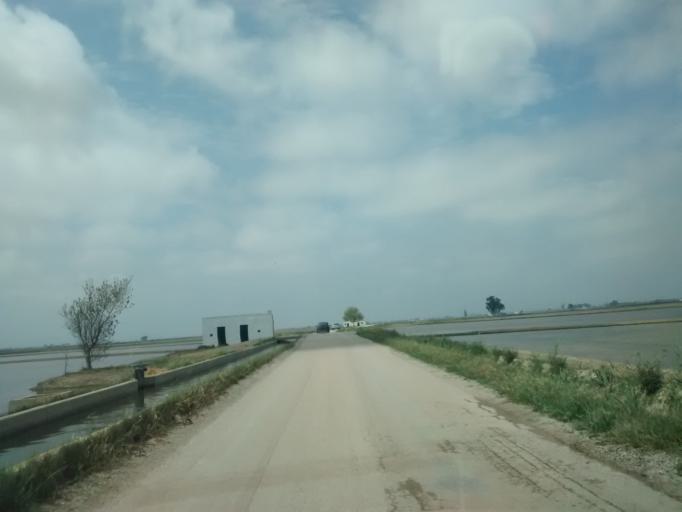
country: ES
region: Catalonia
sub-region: Provincia de Tarragona
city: Deltebre
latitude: 40.6836
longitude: 0.7917
